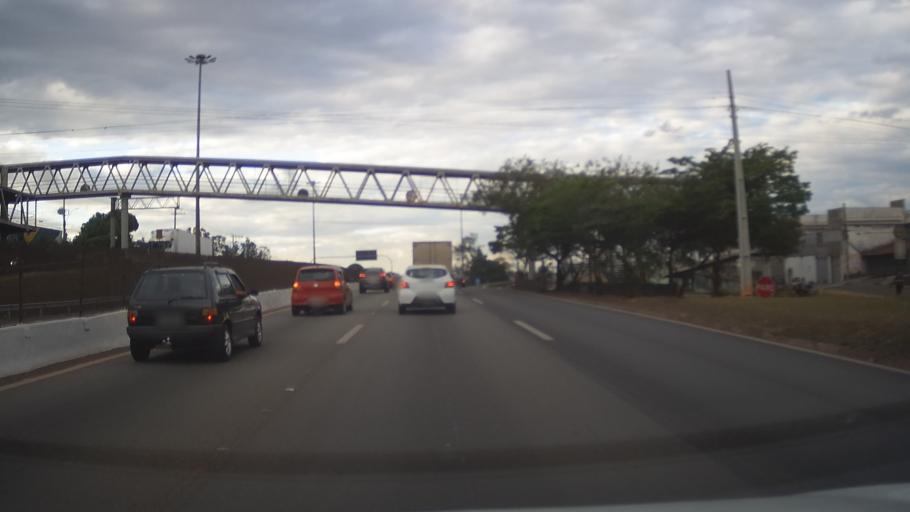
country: BR
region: Minas Gerais
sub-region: Contagem
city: Contagem
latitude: -19.9452
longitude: -44.0079
